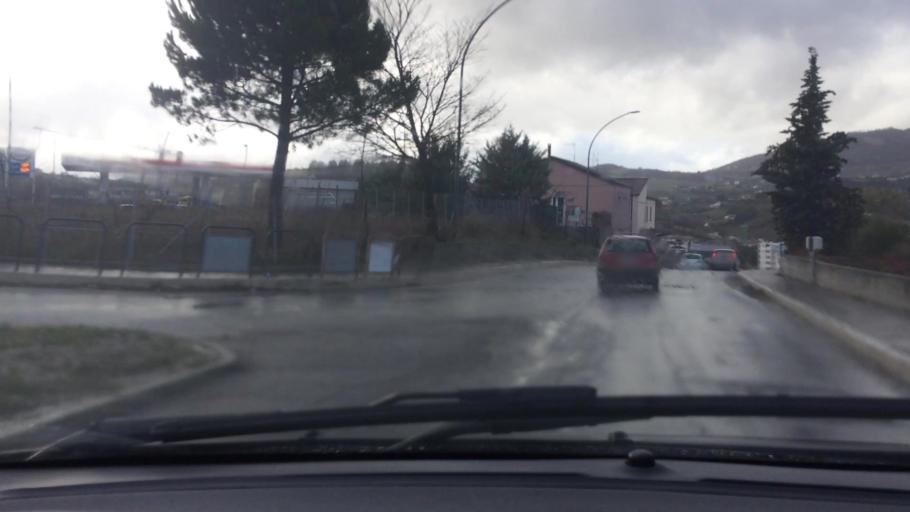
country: IT
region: Basilicate
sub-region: Provincia di Potenza
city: Potenza
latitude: 40.6403
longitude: 15.7884
